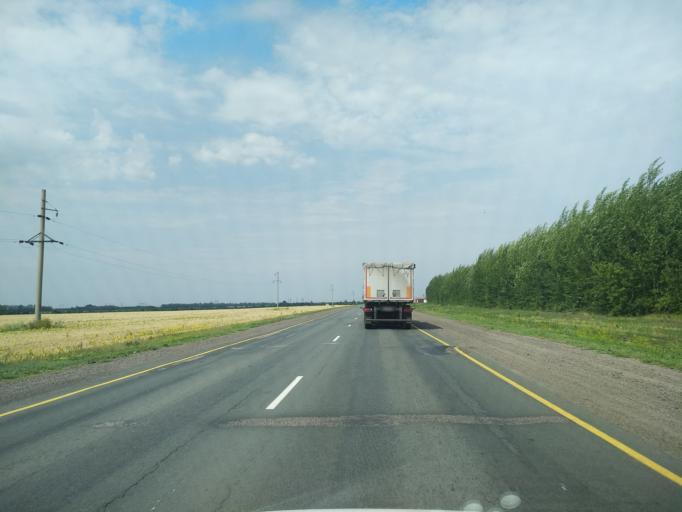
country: RU
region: Voronezj
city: Orlovo
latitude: 51.6771
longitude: 39.6907
